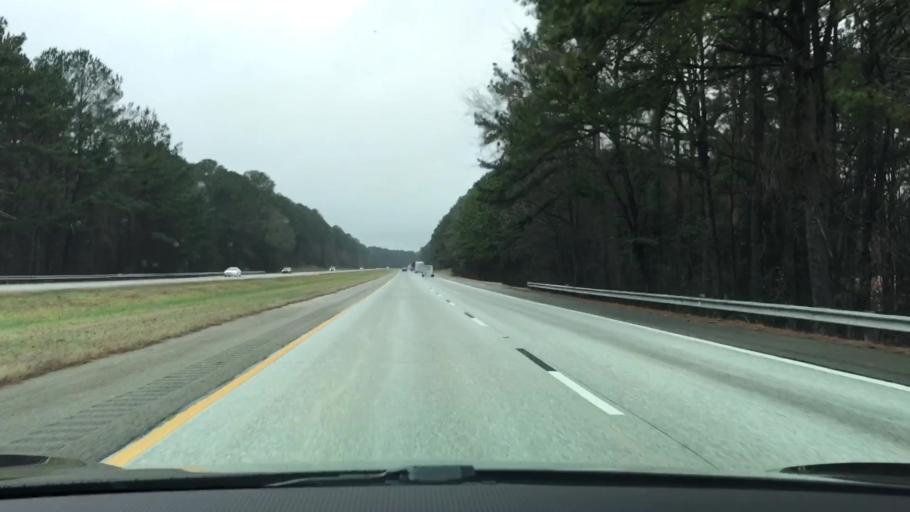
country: US
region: Georgia
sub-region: Putnam County
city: Jefferson
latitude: 33.5337
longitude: -83.2788
